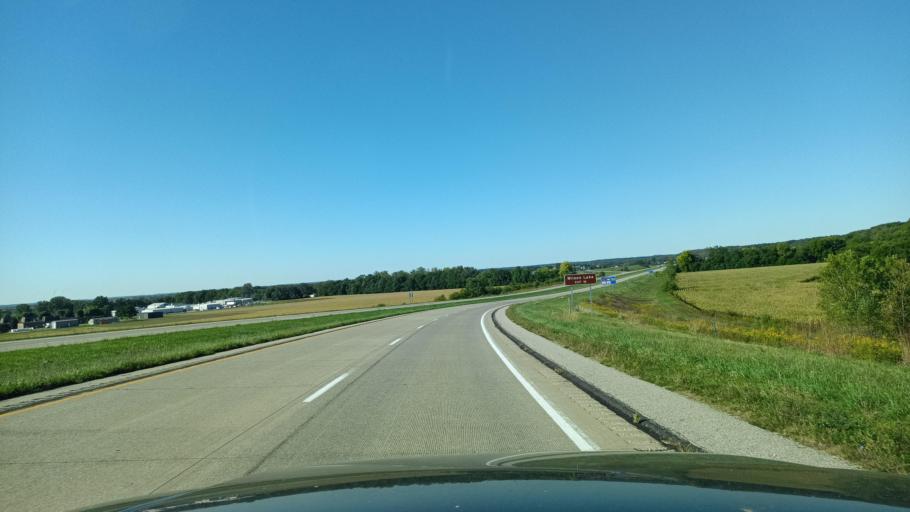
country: US
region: Iowa
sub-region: Lee County
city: Fort Madison
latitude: 40.6318
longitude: -91.3826
